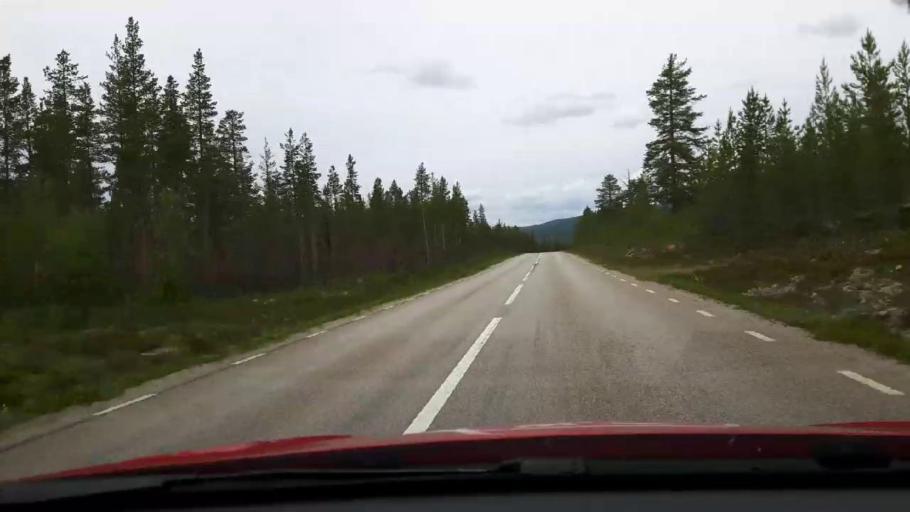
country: SE
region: Jaemtland
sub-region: Harjedalens Kommun
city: Sveg
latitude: 62.2539
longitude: 13.8408
